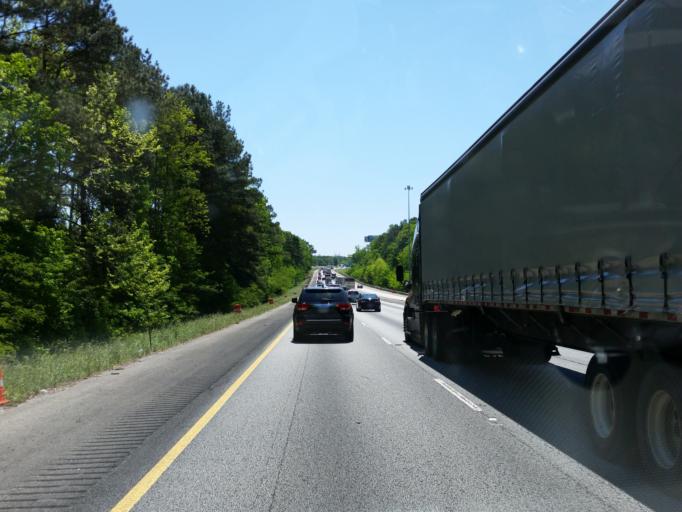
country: US
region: Georgia
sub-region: Henry County
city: Stockbridge
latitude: 33.5022
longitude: -84.2279
